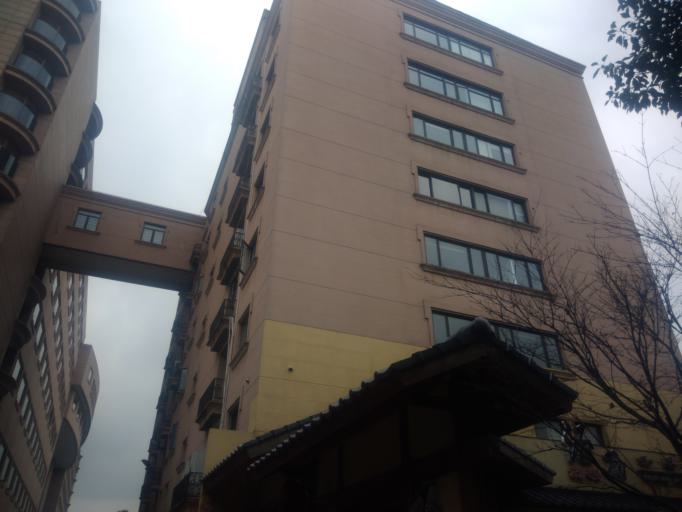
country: CN
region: Shanghai Shi
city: Changzheng
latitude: 31.1924
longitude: 121.3713
